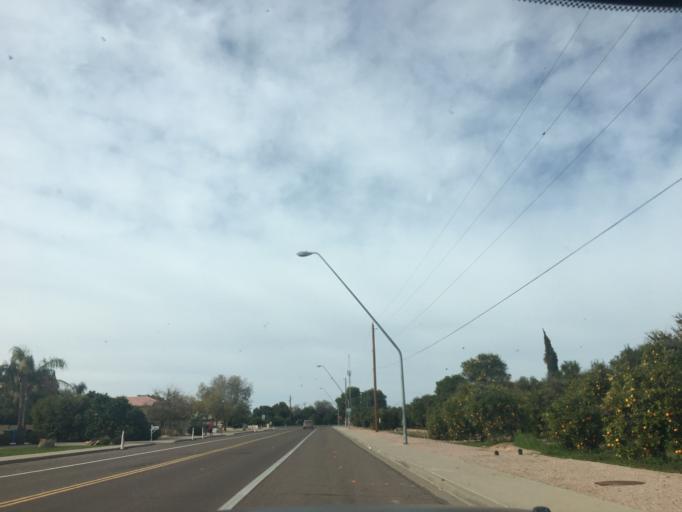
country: US
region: Arizona
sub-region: Maricopa County
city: Mesa
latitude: 33.4591
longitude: -111.7855
